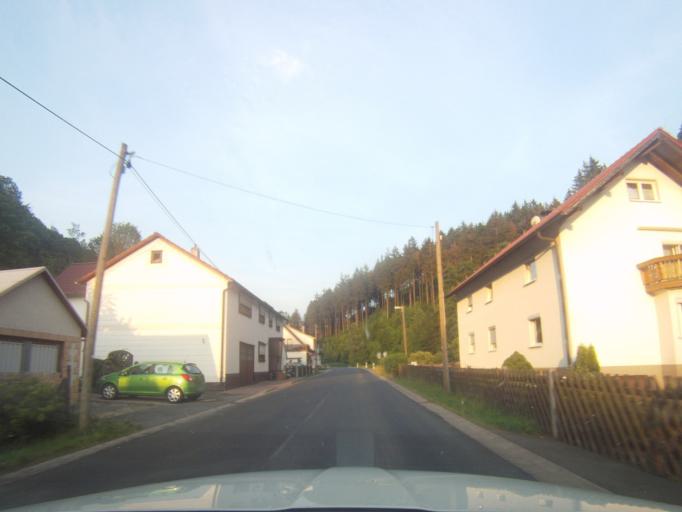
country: DE
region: Thuringia
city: Eisfeld
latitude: 50.4845
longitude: 10.8823
